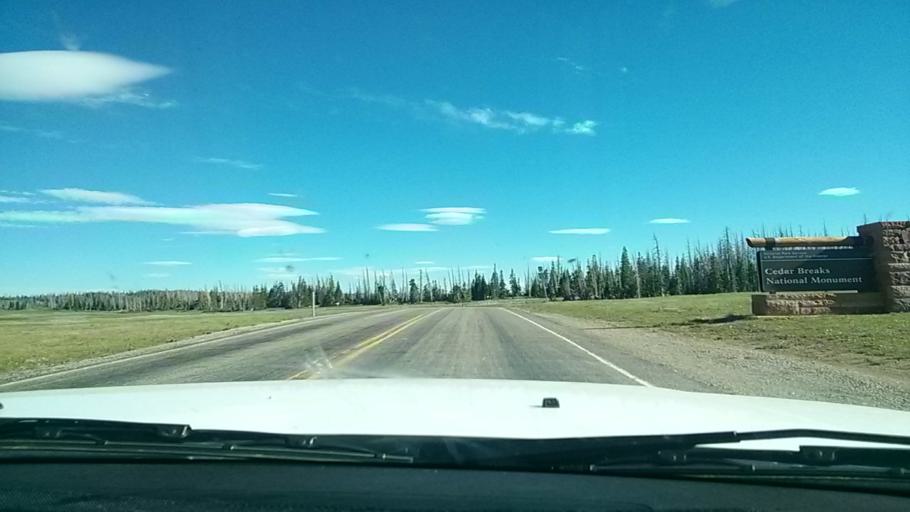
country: US
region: Utah
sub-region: Iron County
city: Parowan
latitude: 37.6623
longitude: -112.8377
